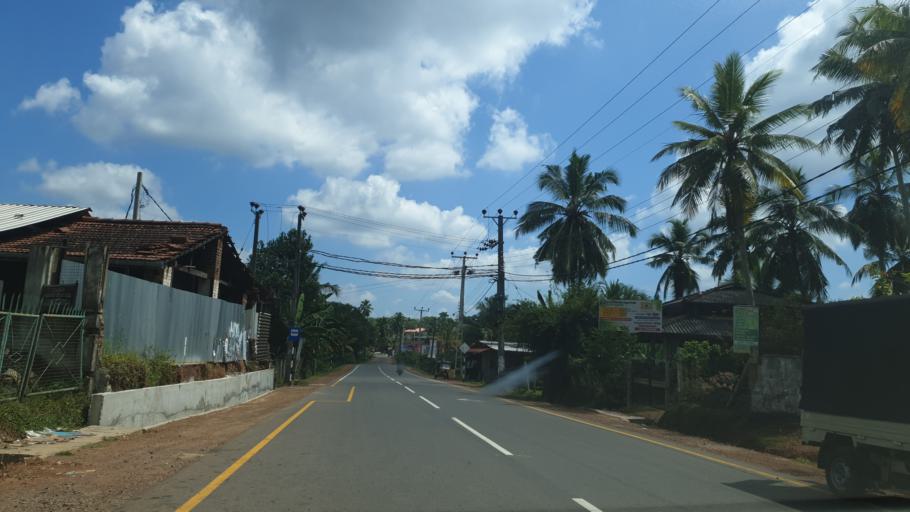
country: LK
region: Western
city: Panadura
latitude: 6.6655
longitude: 79.9563
